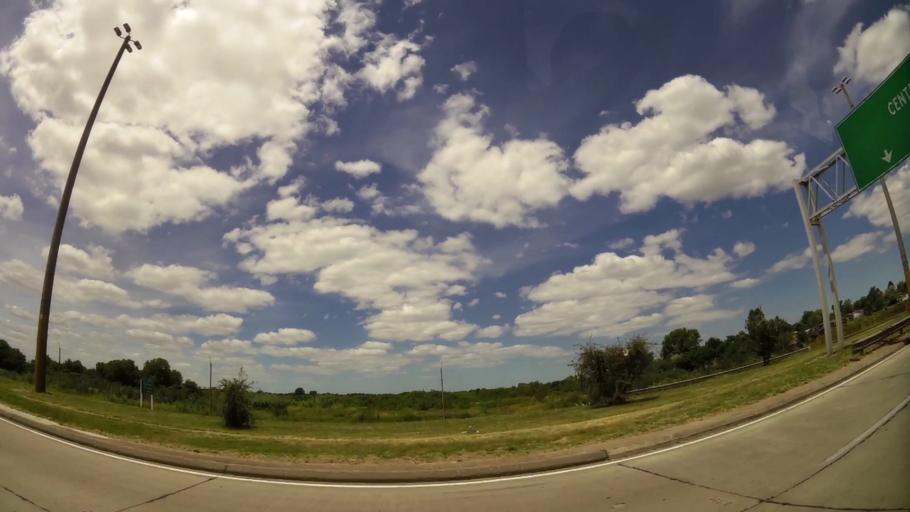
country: UY
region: Montevideo
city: Montevideo
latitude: -34.8543
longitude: -56.2554
